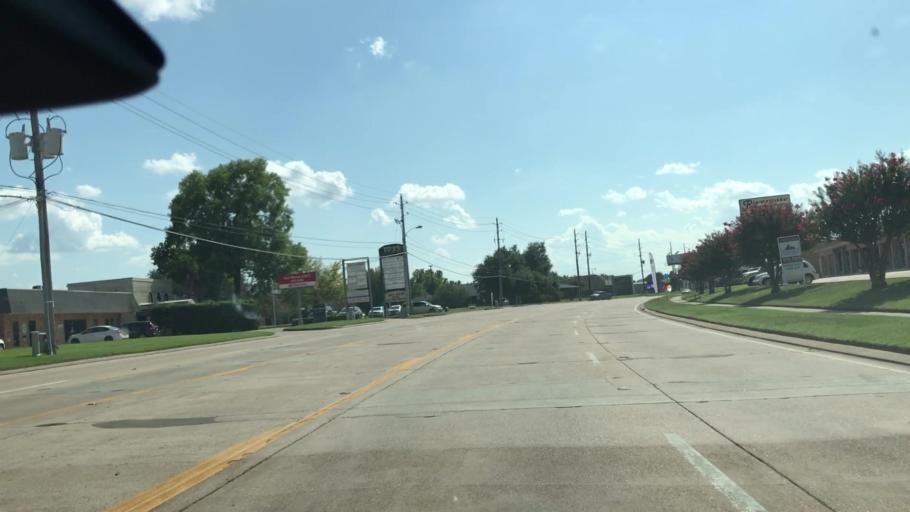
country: US
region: Louisiana
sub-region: Bossier Parish
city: Bossier City
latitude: 32.4441
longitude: -93.7087
